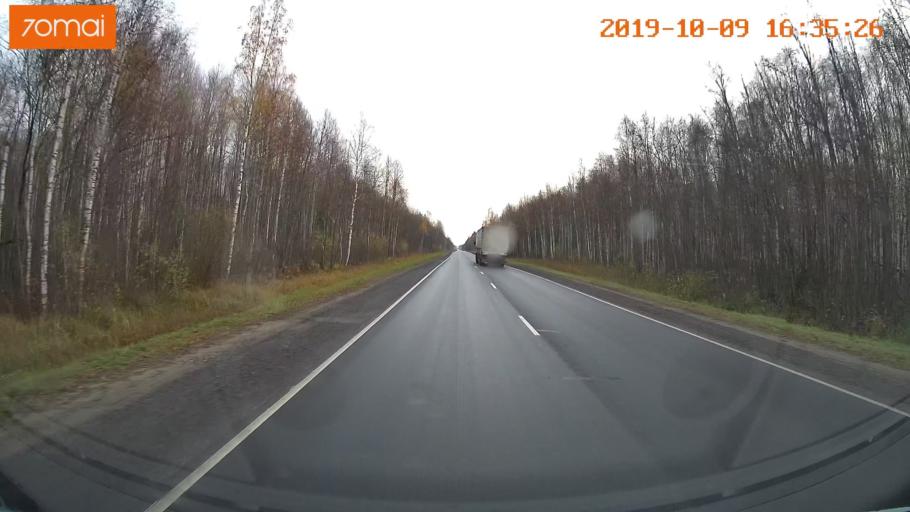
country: RU
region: Kostroma
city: Oktyabr'skiy
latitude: 57.5558
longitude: 41.0008
